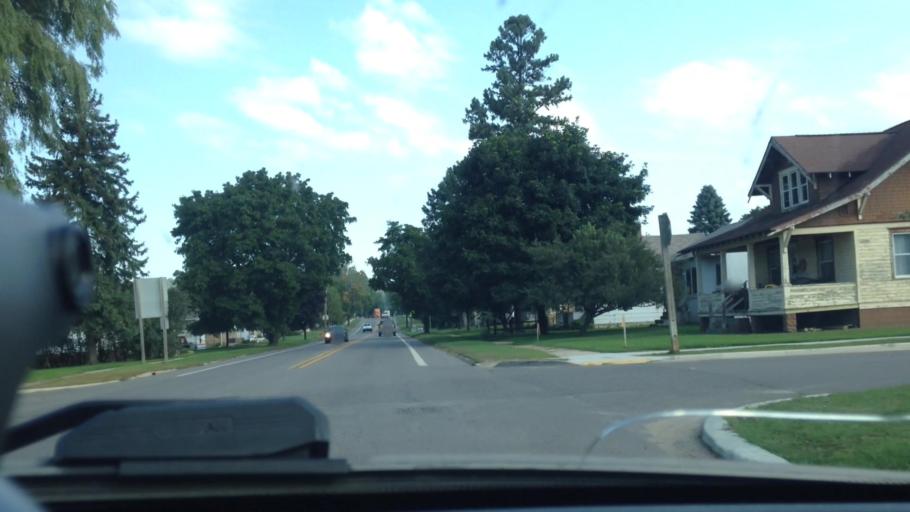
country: US
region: Michigan
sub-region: Dickinson County
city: Norway
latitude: 45.7810
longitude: -87.9098
